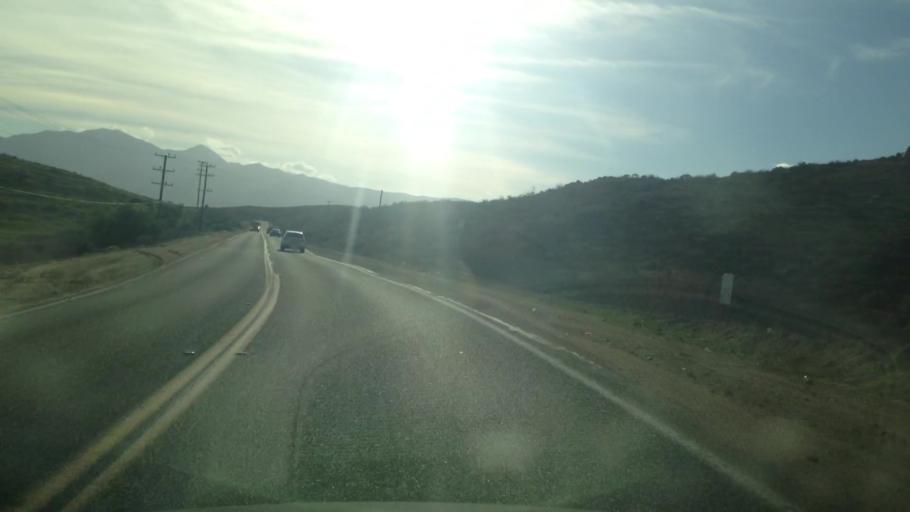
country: US
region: California
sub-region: Riverside County
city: El Cerrito
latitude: 33.8513
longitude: -117.4589
